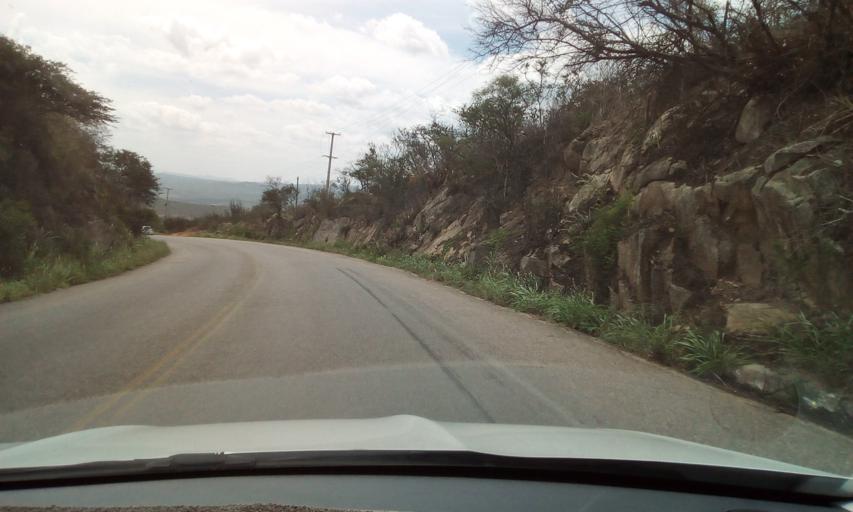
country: BR
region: Pernambuco
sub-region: Bezerros
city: Bezerros
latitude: -8.2741
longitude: -35.7439
